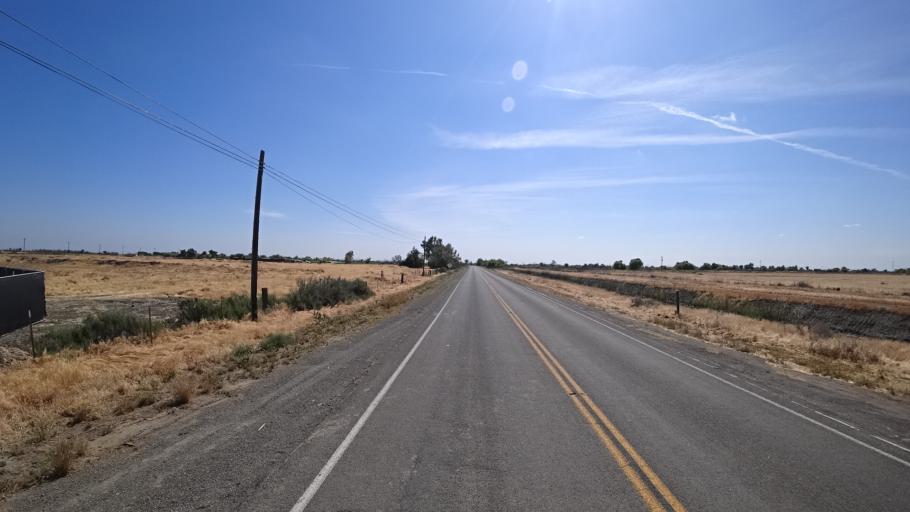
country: US
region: California
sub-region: Kings County
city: Lemoore Station
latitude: 36.2554
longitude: -119.8642
